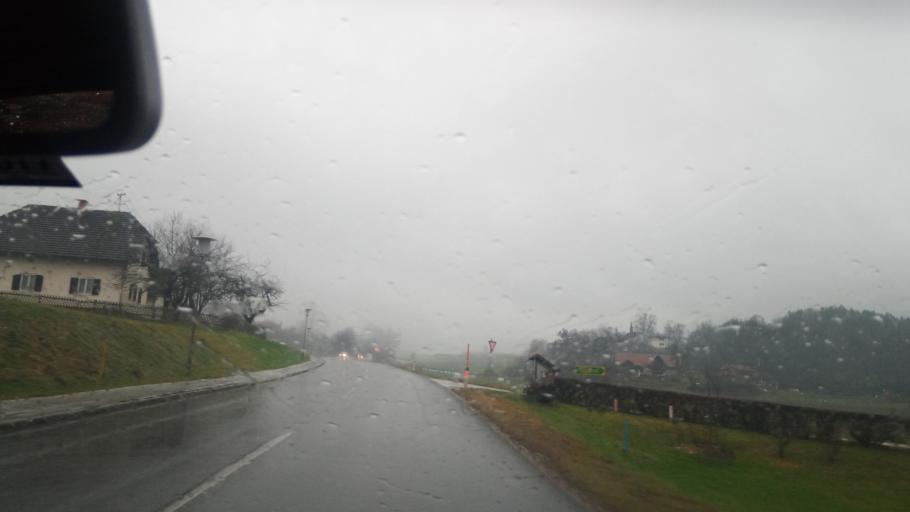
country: AT
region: Carinthia
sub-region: Politischer Bezirk Klagenfurt Land
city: Keutschach am See
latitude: 46.5891
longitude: 14.2179
